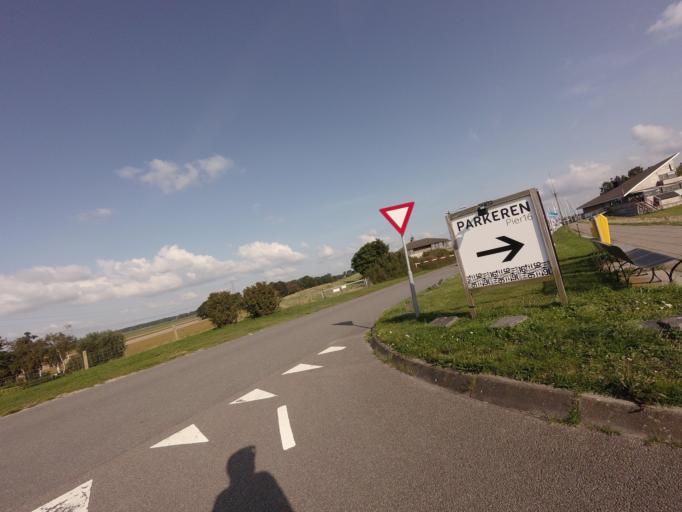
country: NL
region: Flevoland
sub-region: Gemeente Noordoostpolder
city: Ens
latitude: 52.6129
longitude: 5.7439
